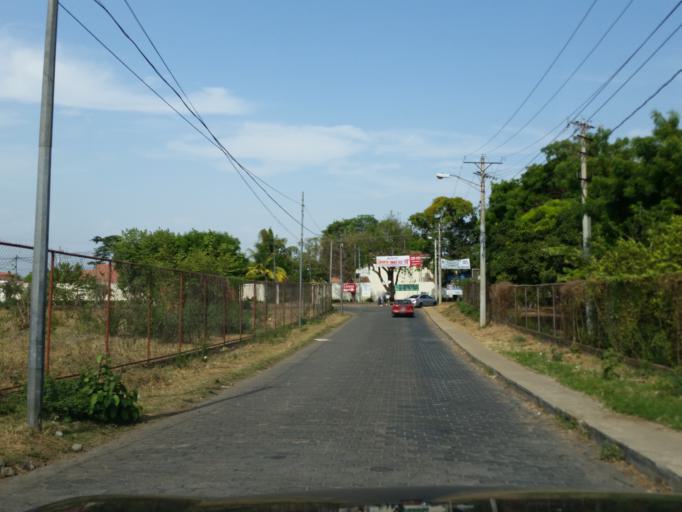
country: NI
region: Managua
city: Managua
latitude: 12.0942
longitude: -86.2253
